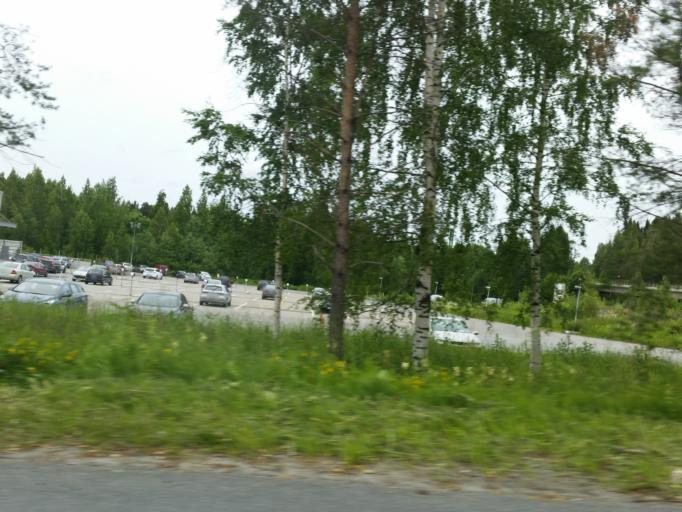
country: FI
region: Northern Savo
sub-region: Kuopio
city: Kuopio
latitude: 62.8828
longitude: 27.6413
